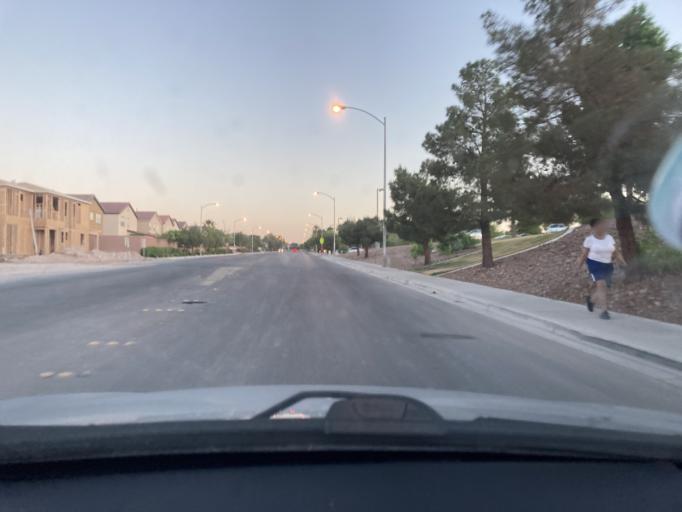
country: US
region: Nevada
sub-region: Clark County
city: Enterprise
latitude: 36.0618
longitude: -115.2884
